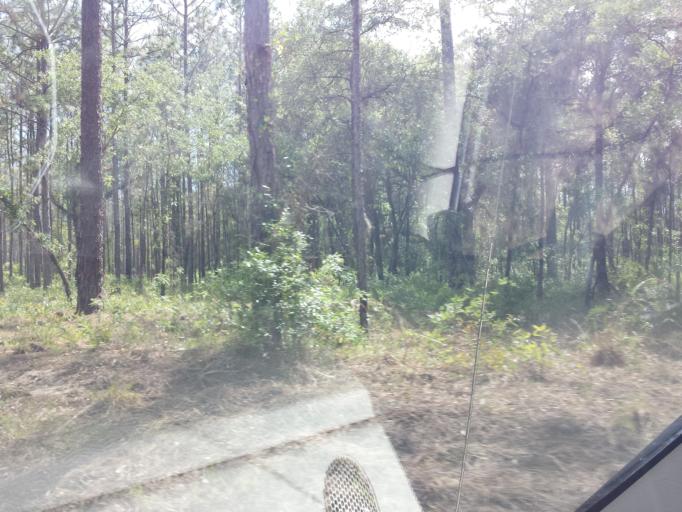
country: US
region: Florida
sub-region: Hernando County
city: Hill 'n Dale
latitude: 28.5581
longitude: -82.2679
